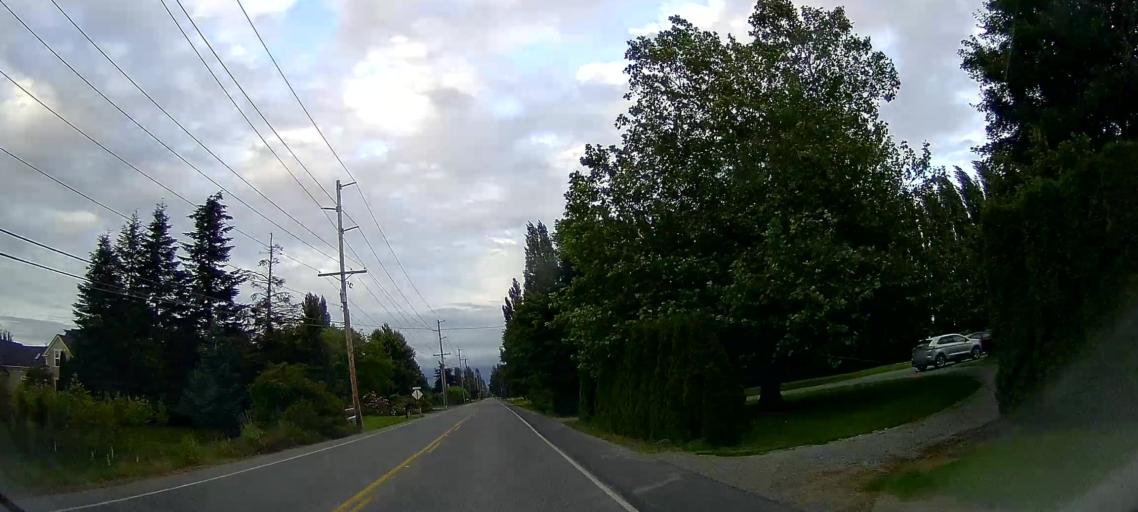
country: US
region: Washington
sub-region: Skagit County
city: Mount Vernon
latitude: 48.4211
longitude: -122.4200
